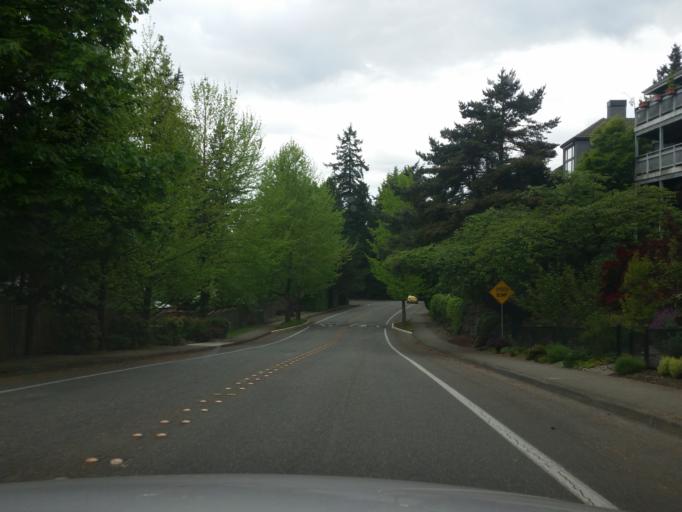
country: US
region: Washington
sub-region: King County
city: Yarrow Point
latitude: 47.6433
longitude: -122.1906
